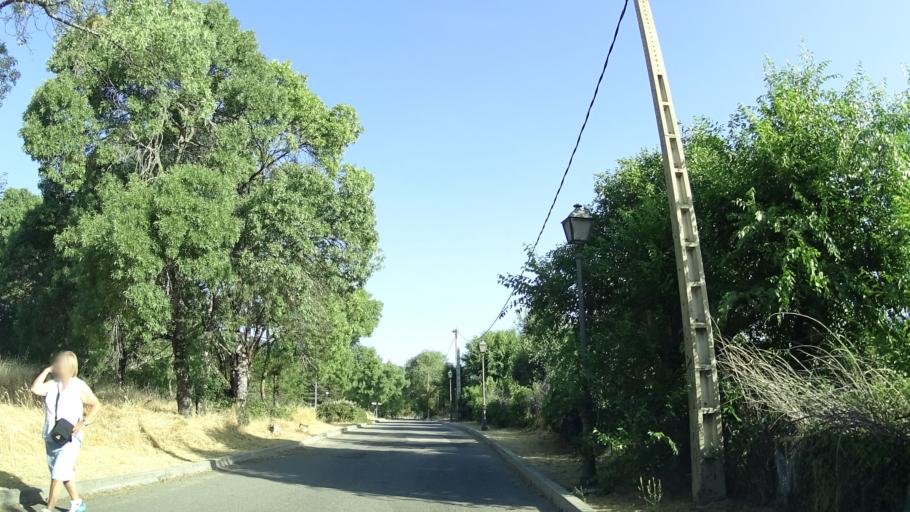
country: ES
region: Madrid
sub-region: Provincia de Madrid
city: Guadarrama
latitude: 40.6779
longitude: -4.1015
